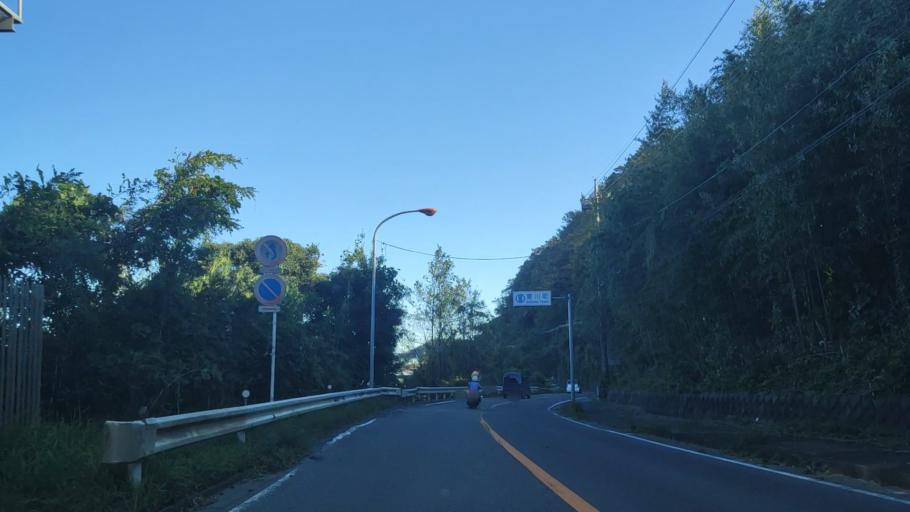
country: JP
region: Kanagawa
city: Zama
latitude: 35.5426
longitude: 139.3258
